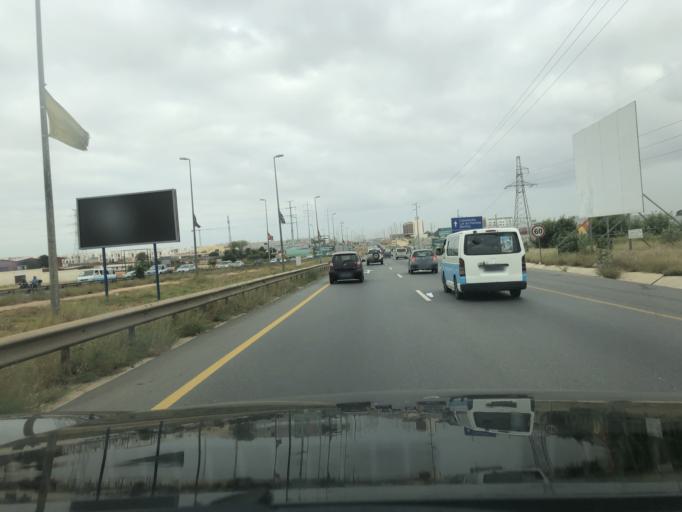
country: AO
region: Luanda
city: Luanda
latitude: -8.9738
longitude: 13.2248
